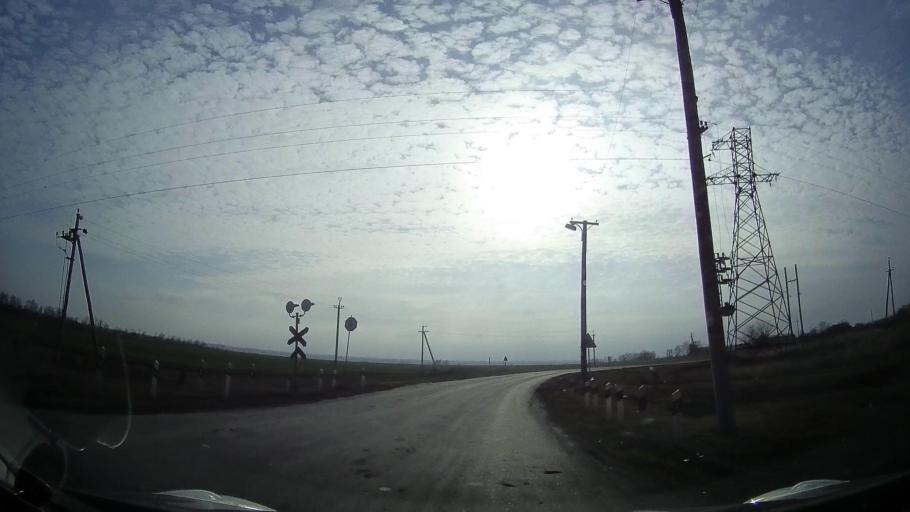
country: RU
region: Rostov
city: Mechetinskaya
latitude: 46.7864
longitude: 40.4832
